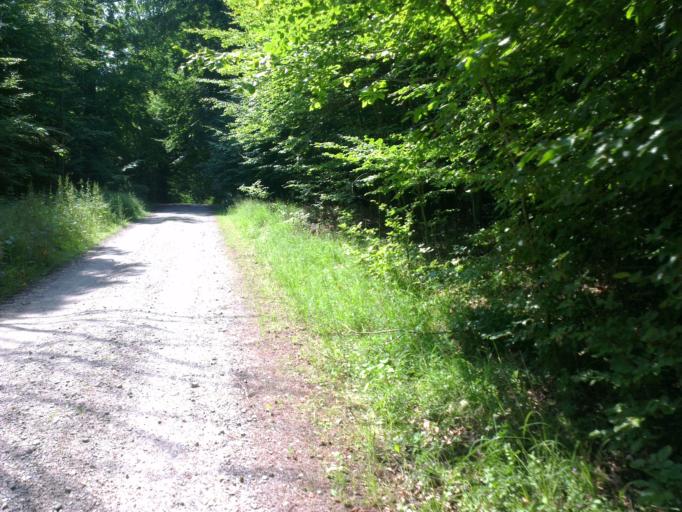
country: DK
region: Capital Region
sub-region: Allerod Kommune
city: Lillerod
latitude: 55.9226
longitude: 12.3611
